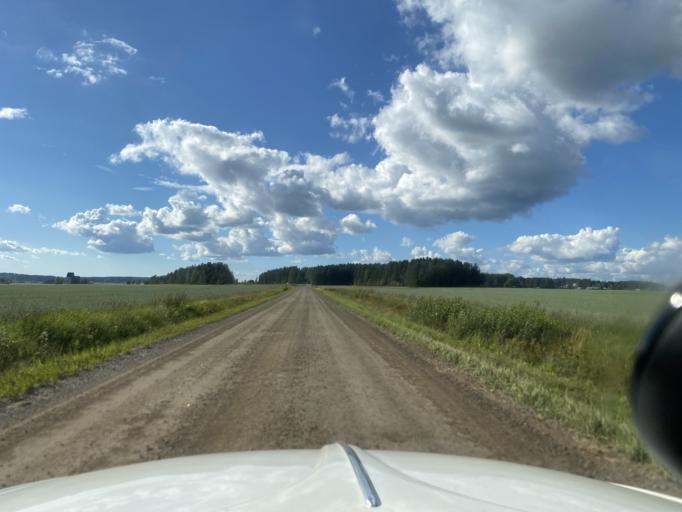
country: FI
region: Pirkanmaa
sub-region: Lounais-Pirkanmaa
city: Punkalaidun
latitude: 61.1348
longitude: 23.2271
